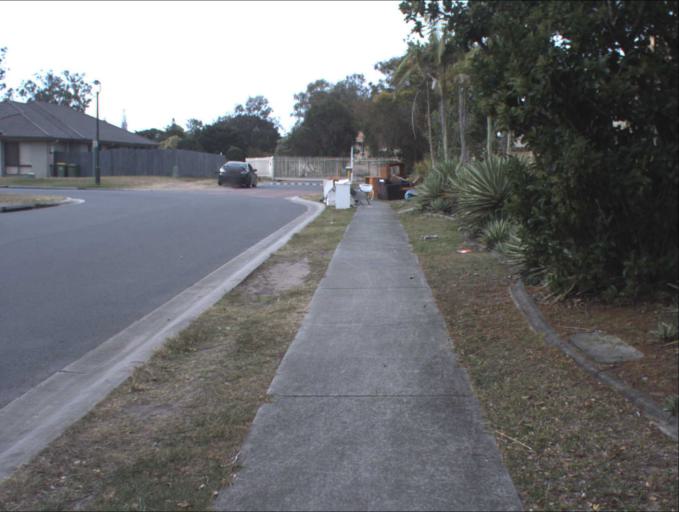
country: AU
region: Queensland
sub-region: Logan
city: Logan City
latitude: -27.6308
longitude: 153.1239
